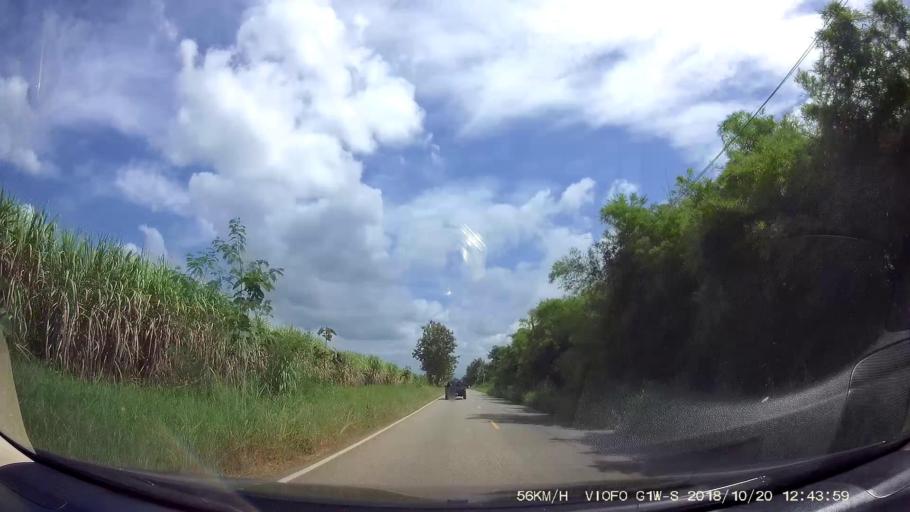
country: TH
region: Chaiyaphum
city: Khon San
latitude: 16.5403
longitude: 101.8653
